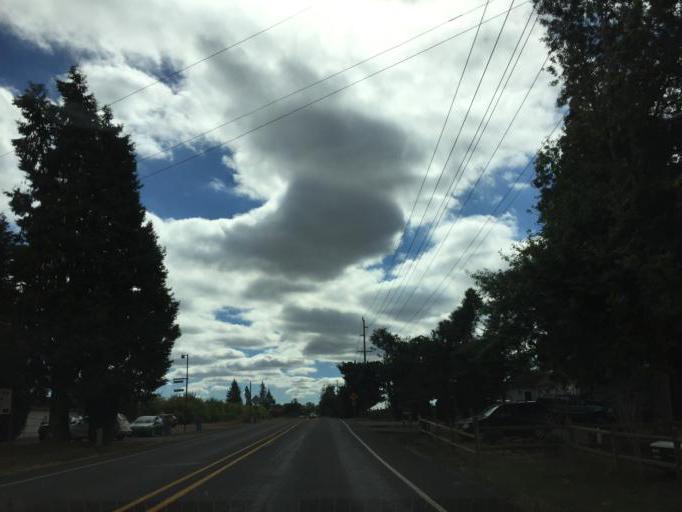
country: US
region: Oregon
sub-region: Marion County
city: Woodburn
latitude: 45.1248
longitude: -122.8050
